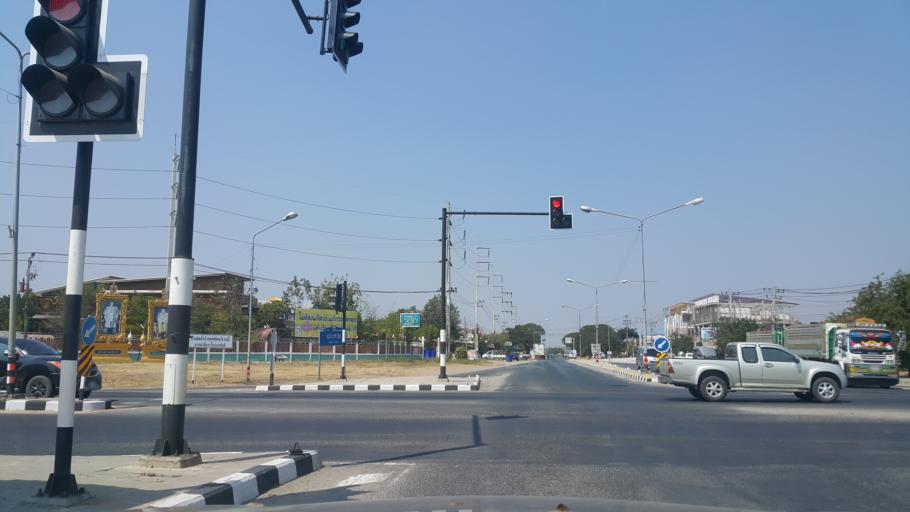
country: TH
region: Nakhon Ratchasima
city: Prathai
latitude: 15.5289
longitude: 102.7134
